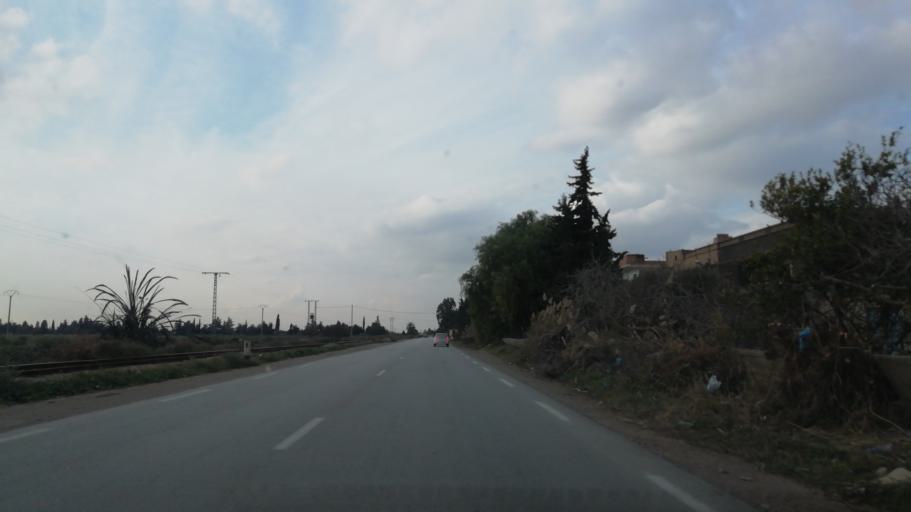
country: DZ
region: Mascara
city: Sig
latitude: 35.6621
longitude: 0.0064
